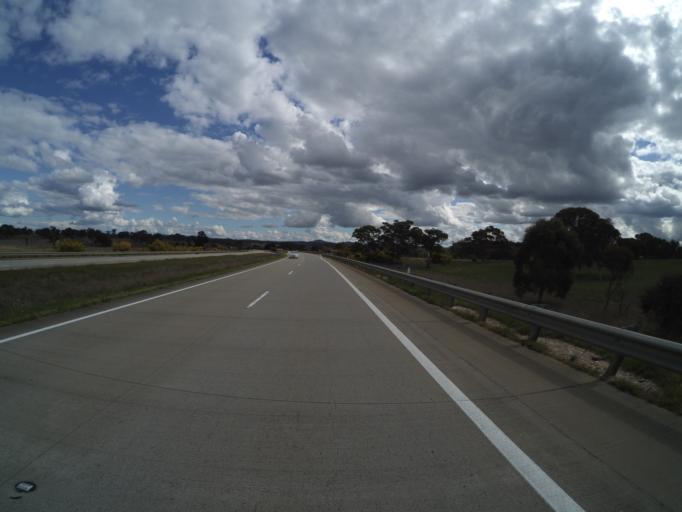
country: AU
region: New South Wales
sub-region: Yass Valley
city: Murrumbateman
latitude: -34.8011
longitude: 149.1396
